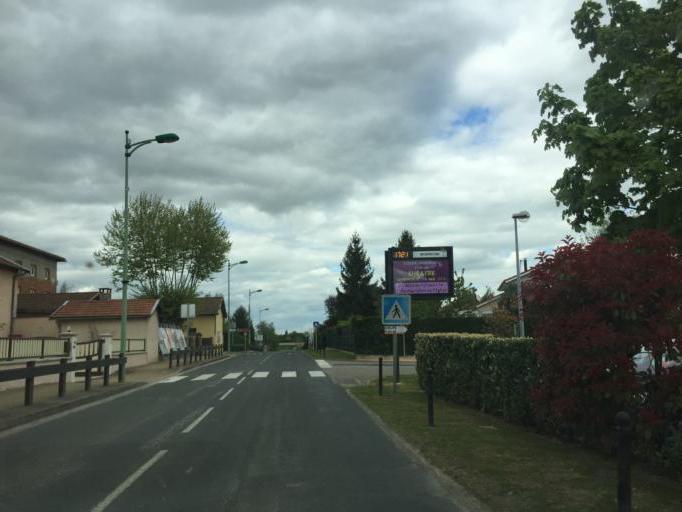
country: FR
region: Rhone-Alpes
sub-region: Departement de l'Ain
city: Saint-Andre-de-Corcy
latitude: 45.9575
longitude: 4.9406
